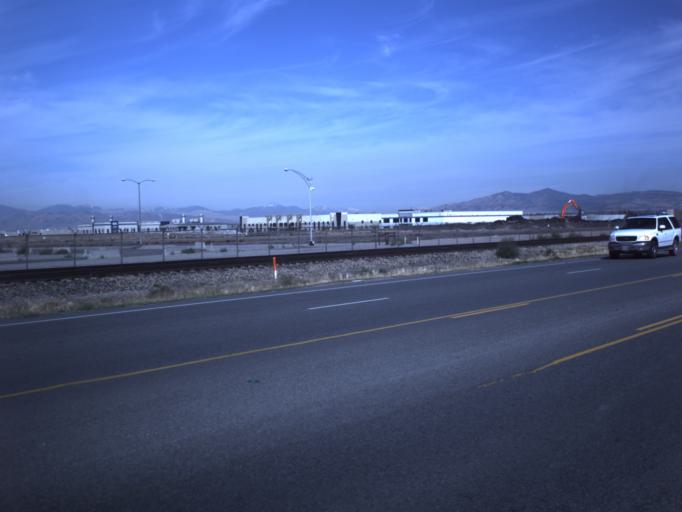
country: US
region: Utah
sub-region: Utah County
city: Lindon
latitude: 40.3225
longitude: -111.7365
